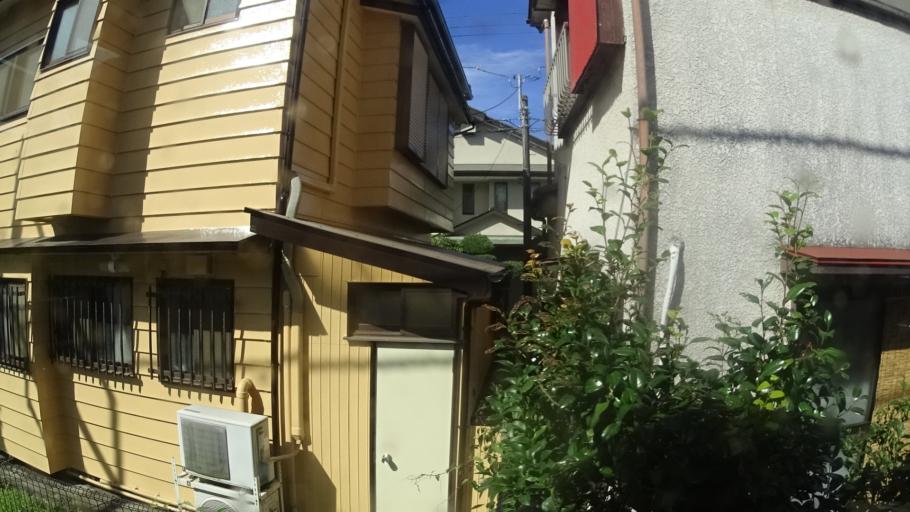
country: JP
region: Kanagawa
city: Fujisawa
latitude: 35.3157
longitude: 139.4824
